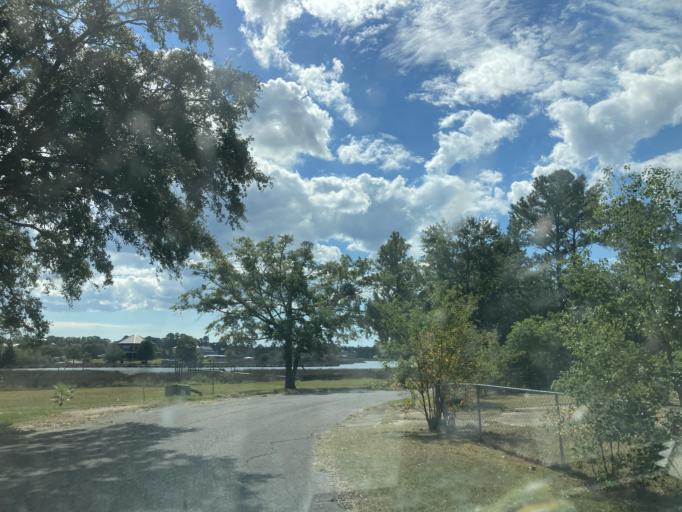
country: US
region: Mississippi
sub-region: Jackson County
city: Gulf Hills
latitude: 30.4374
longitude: -88.8497
